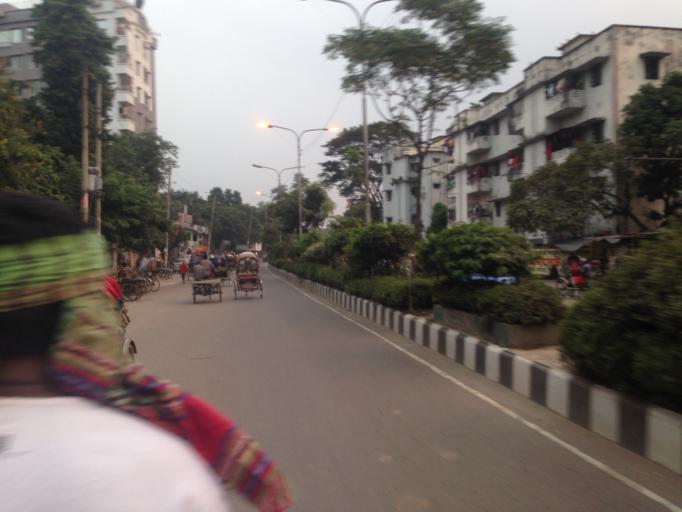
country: BD
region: Dhaka
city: Paltan
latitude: 23.7374
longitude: 90.4227
